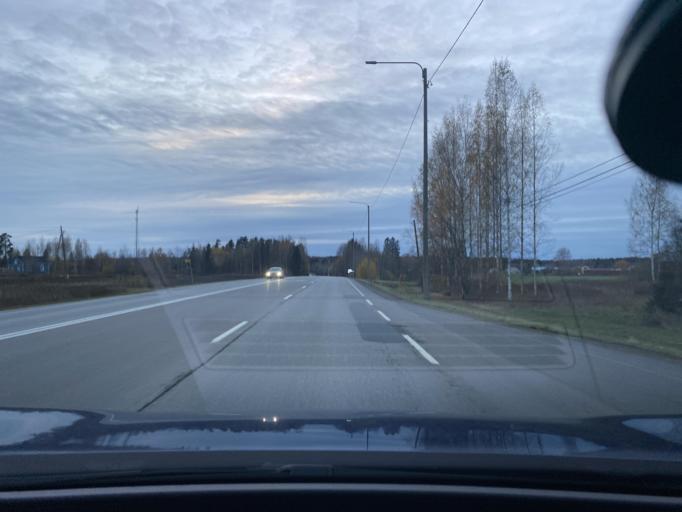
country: FI
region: Uusimaa
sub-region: Helsinki
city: Saukkola
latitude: 60.3864
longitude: 24.0058
